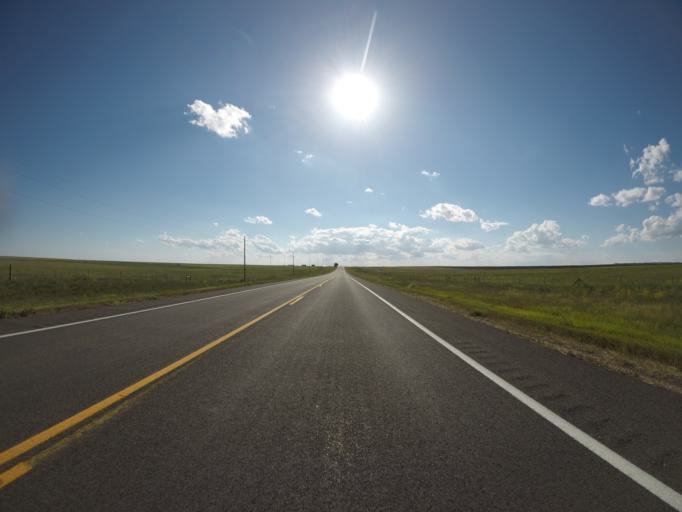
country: US
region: Colorado
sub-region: Morgan County
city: Fort Morgan
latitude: 40.6113
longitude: -103.8104
